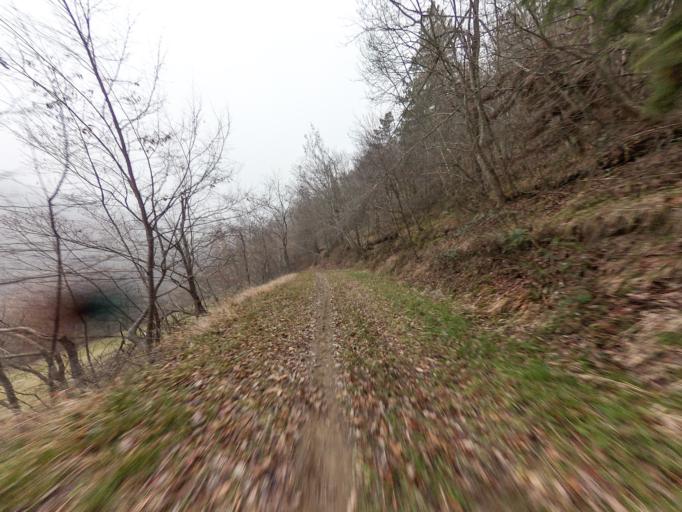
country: IT
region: Emilia-Romagna
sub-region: Provincia di Bologna
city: Pianoro
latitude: 44.3403
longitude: 11.3203
